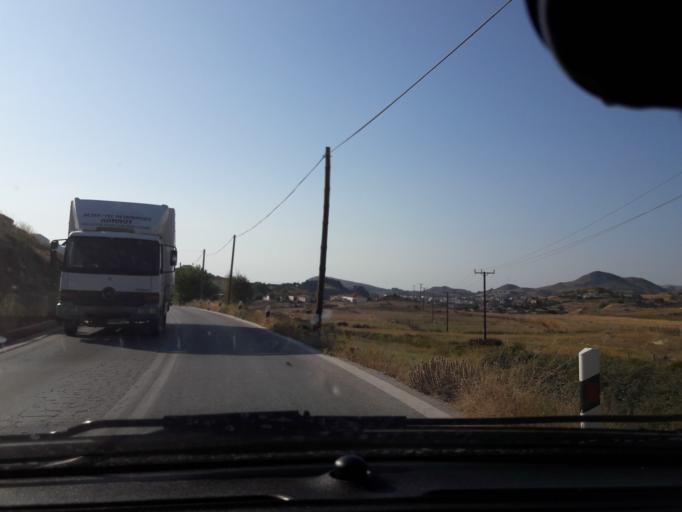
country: GR
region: North Aegean
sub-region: Nomos Lesvou
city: Myrina
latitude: 39.8689
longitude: 25.0724
